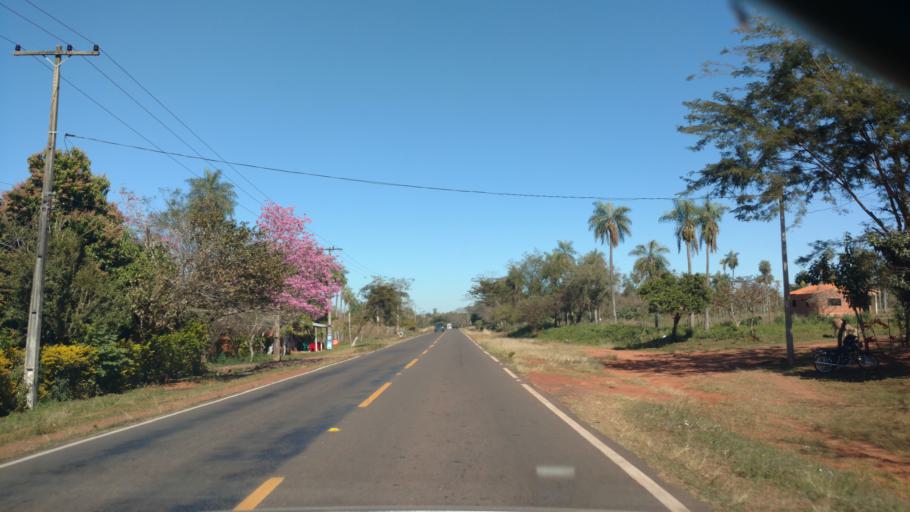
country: PY
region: Paraguari
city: Pirayu
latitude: -25.5215
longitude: -57.2658
